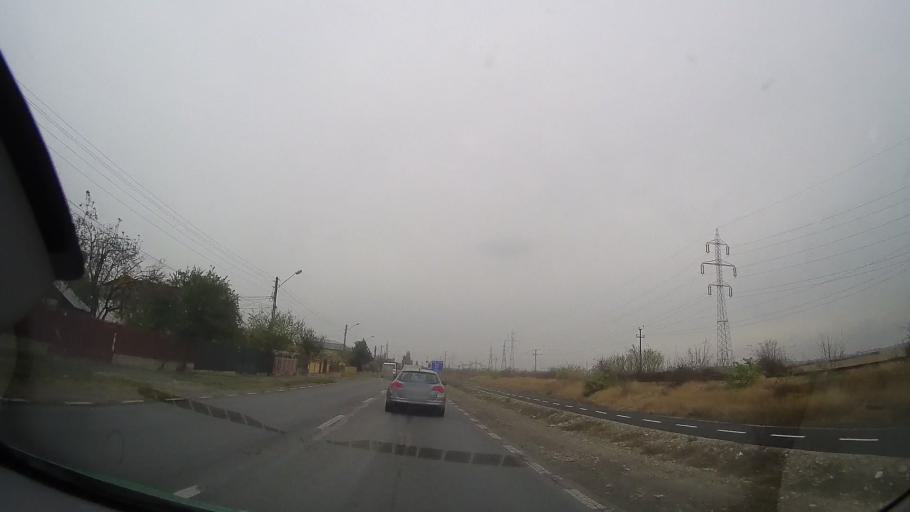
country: RO
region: Prahova
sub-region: Comuna Blejoiu
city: Ploiestiori
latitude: 44.9782
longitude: 26.0171
